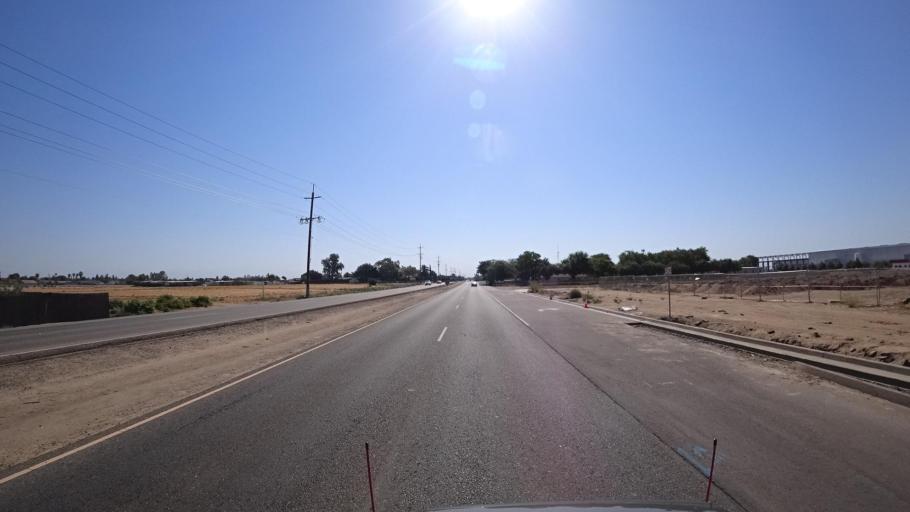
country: US
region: California
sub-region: Fresno County
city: Sunnyside
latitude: 36.7070
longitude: -119.7344
